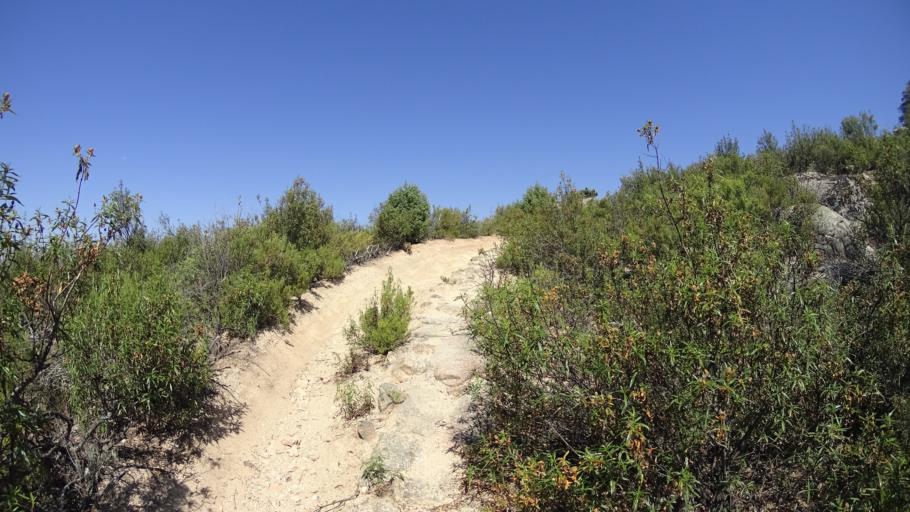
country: ES
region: Madrid
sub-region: Provincia de Madrid
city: Hoyo de Manzanares
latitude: 40.6411
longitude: -3.9353
